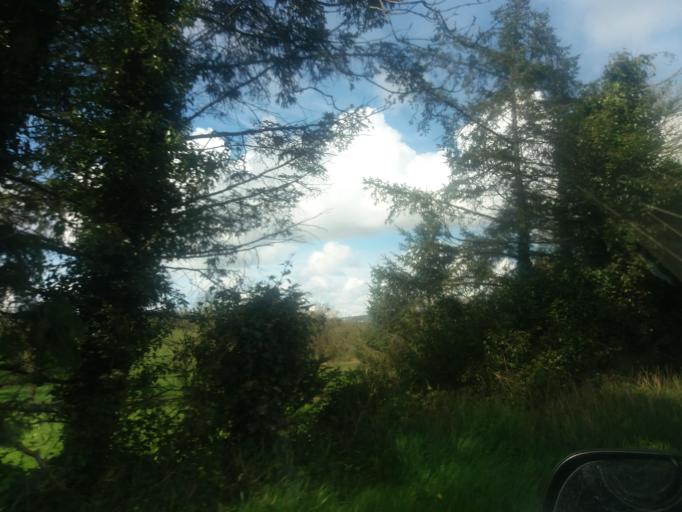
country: IE
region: Ulster
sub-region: An Cabhan
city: Belturbet
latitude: 54.1380
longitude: -7.5044
